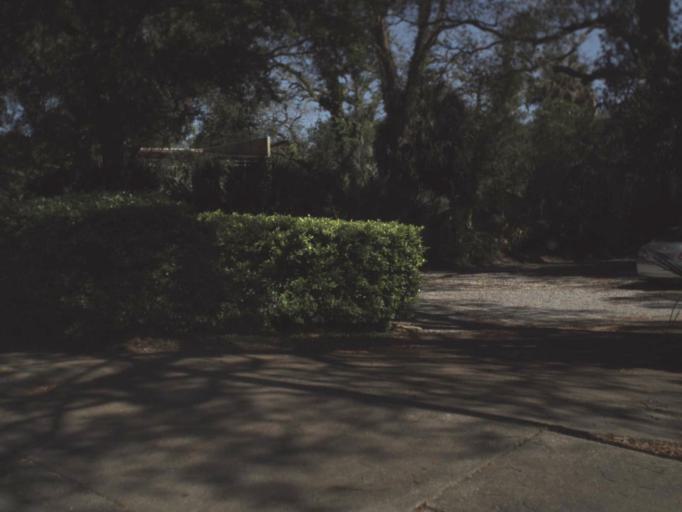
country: US
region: Florida
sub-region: Escambia County
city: Pensacola
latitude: 30.4209
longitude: -87.2197
